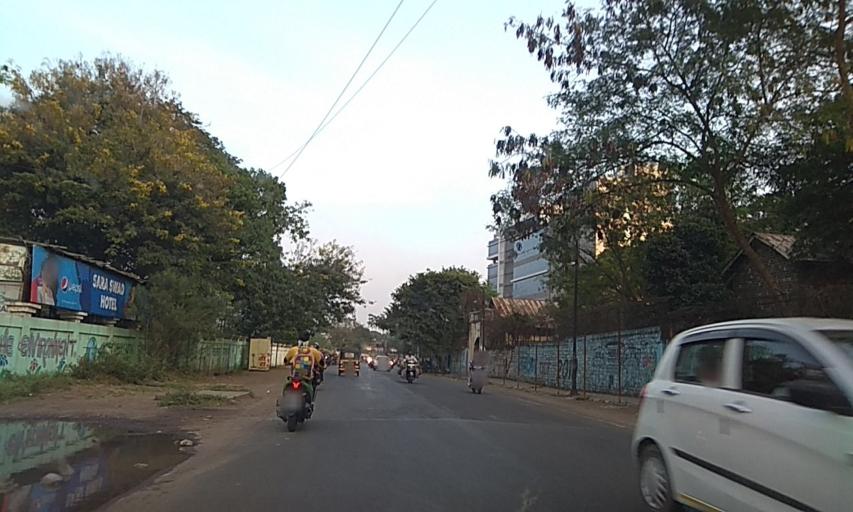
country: IN
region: Maharashtra
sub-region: Pune Division
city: Khadki
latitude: 18.5645
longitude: 73.8825
